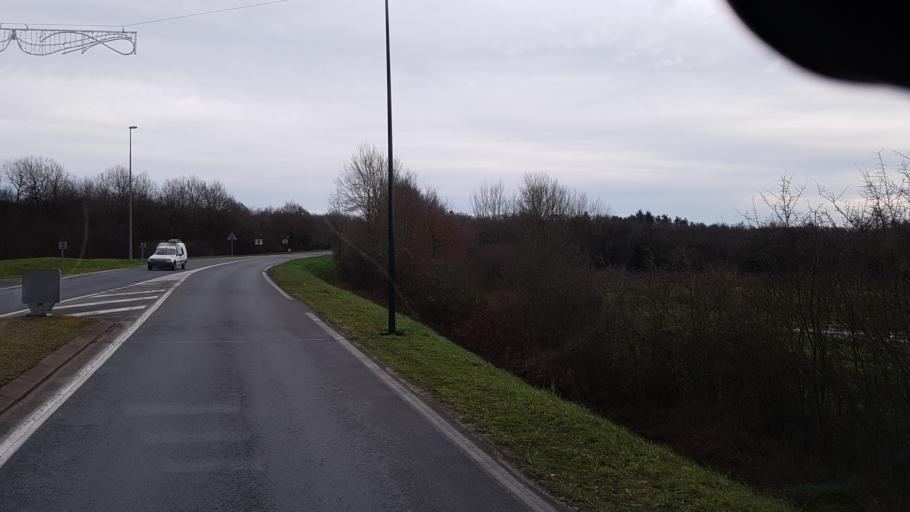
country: FR
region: Centre
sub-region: Departement du Loiret
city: La Ferte-Saint-Aubin
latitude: 47.7044
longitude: 1.9452
